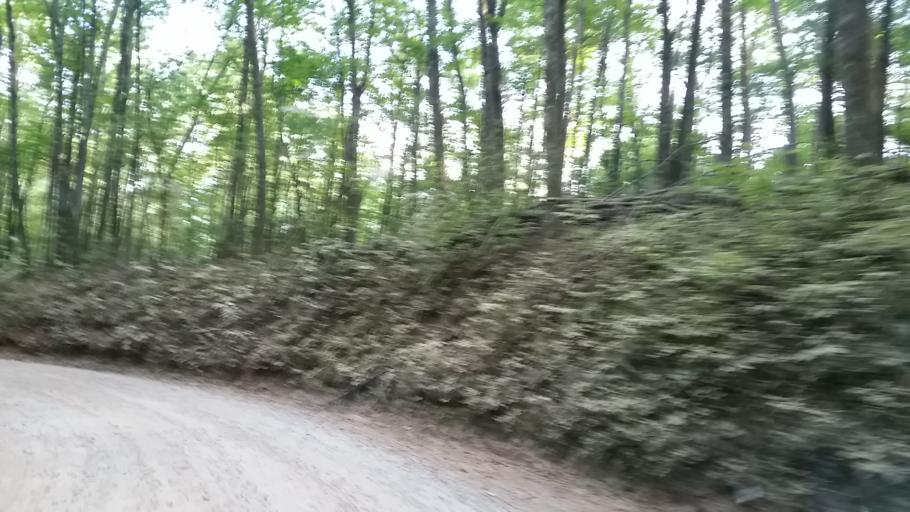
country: US
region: Georgia
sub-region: Lumpkin County
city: Dahlonega
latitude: 34.6295
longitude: -84.1017
